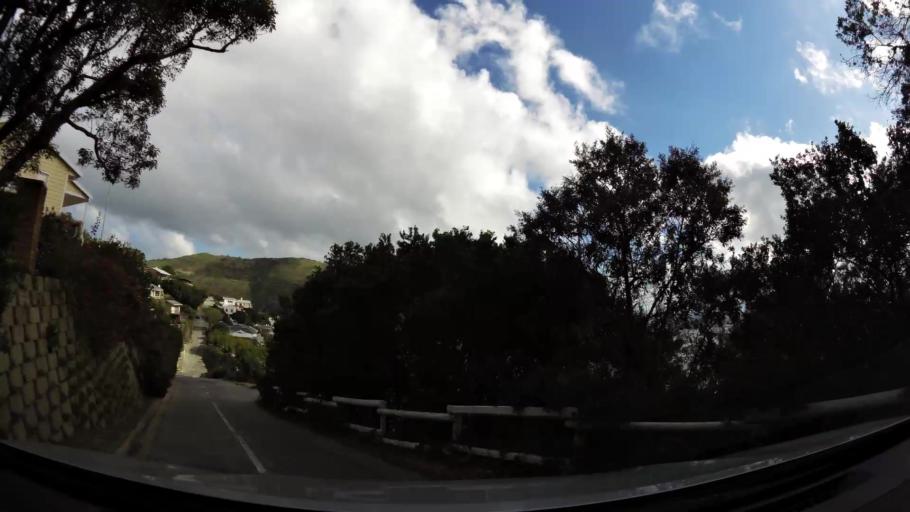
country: ZA
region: Western Cape
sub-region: Eden District Municipality
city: Knysna
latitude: -34.0768
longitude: 23.0649
